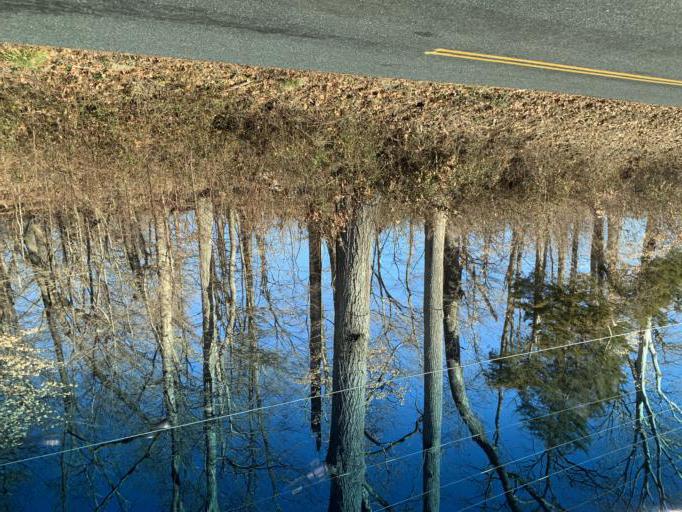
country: US
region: Maryland
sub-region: Harford County
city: Riverside
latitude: 39.5350
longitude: -76.2543
